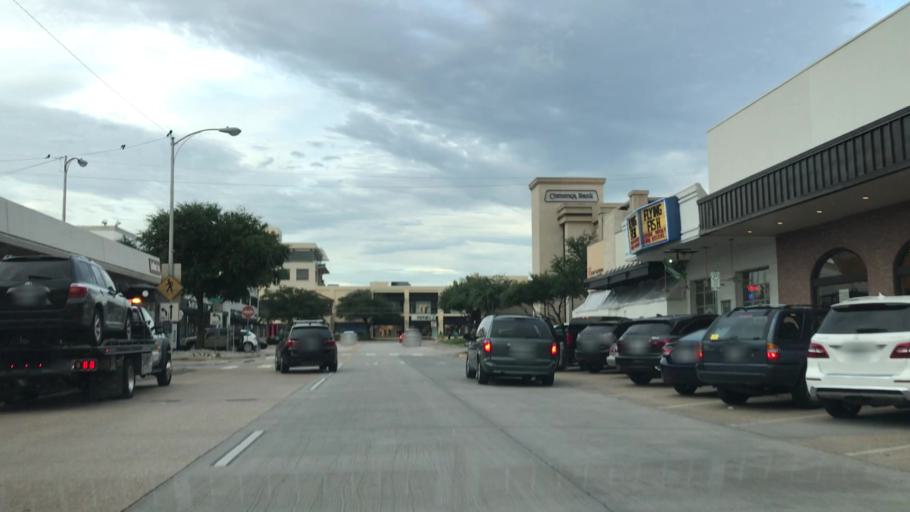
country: US
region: Texas
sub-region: Dallas County
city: University Park
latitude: 32.8636
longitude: -96.8058
